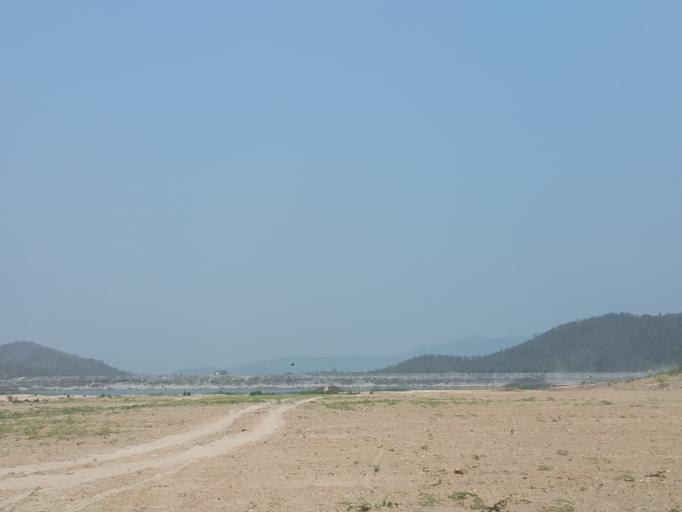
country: TH
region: Chiang Mai
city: Mae On
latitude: 18.6985
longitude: 99.2046
